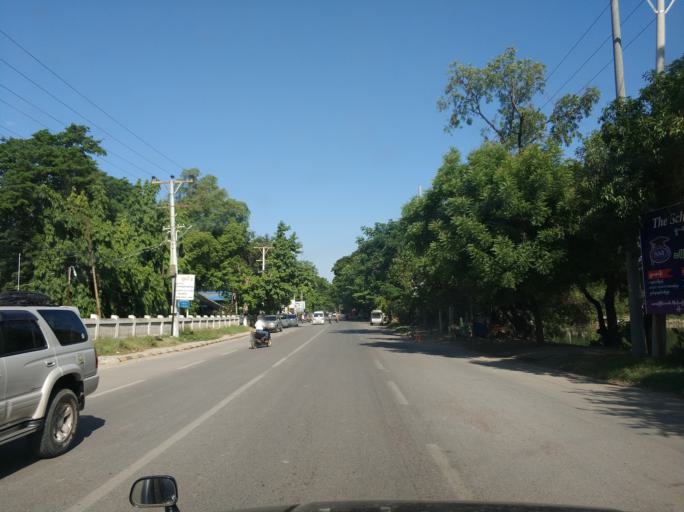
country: MM
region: Mandalay
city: Mandalay
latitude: 21.9711
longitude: 96.0611
